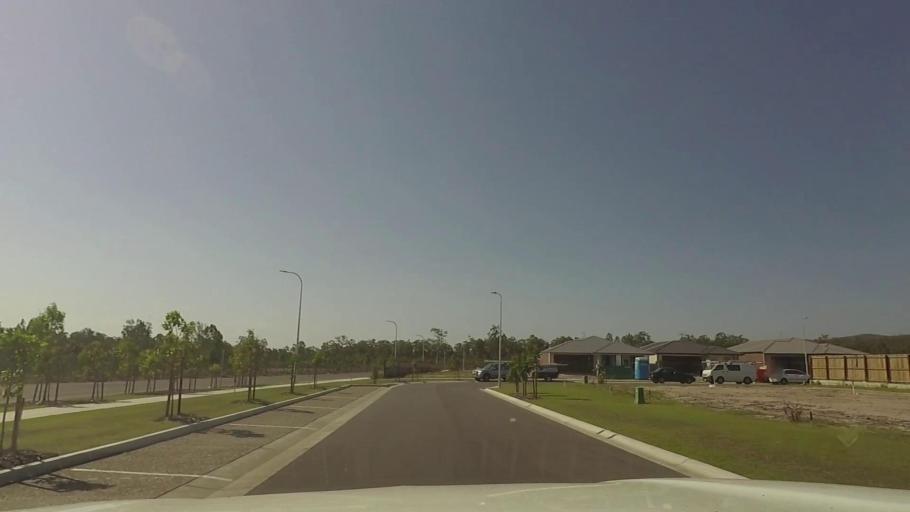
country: AU
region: Queensland
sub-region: Logan
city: Chambers Flat
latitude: -27.8162
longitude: 153.1278
